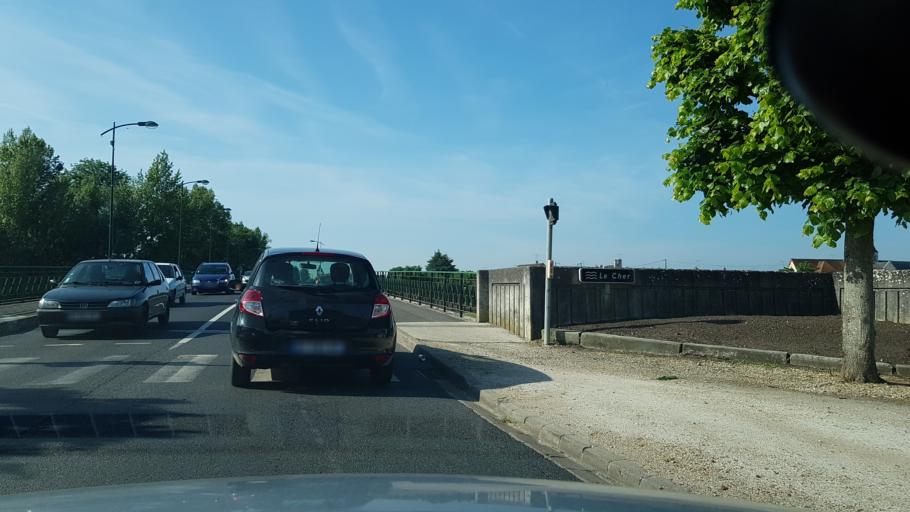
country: FR
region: Centre
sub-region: Departement du Loir-et-Cher
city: Selles-sur-Cher
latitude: 47.2788
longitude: 1.5579
